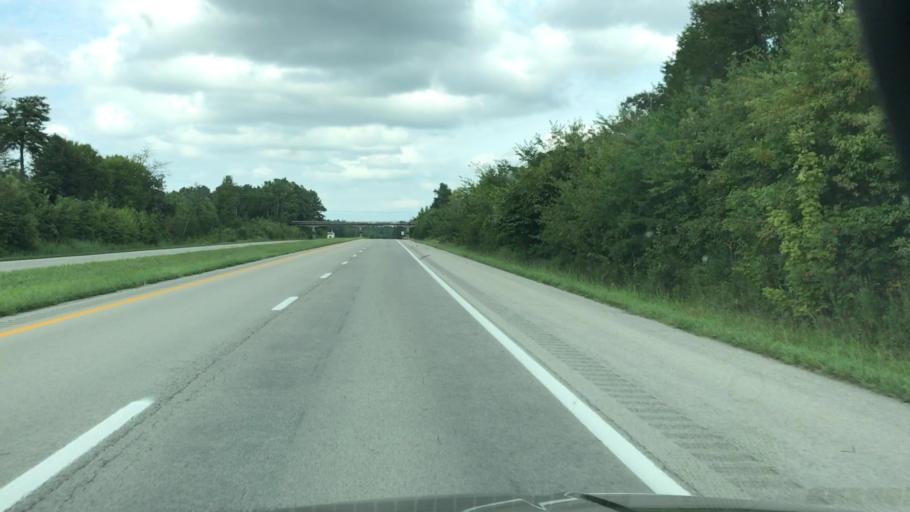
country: US
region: Kentucky
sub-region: Caldwell County
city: Princeton
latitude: 37.1454
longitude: -87.8020
